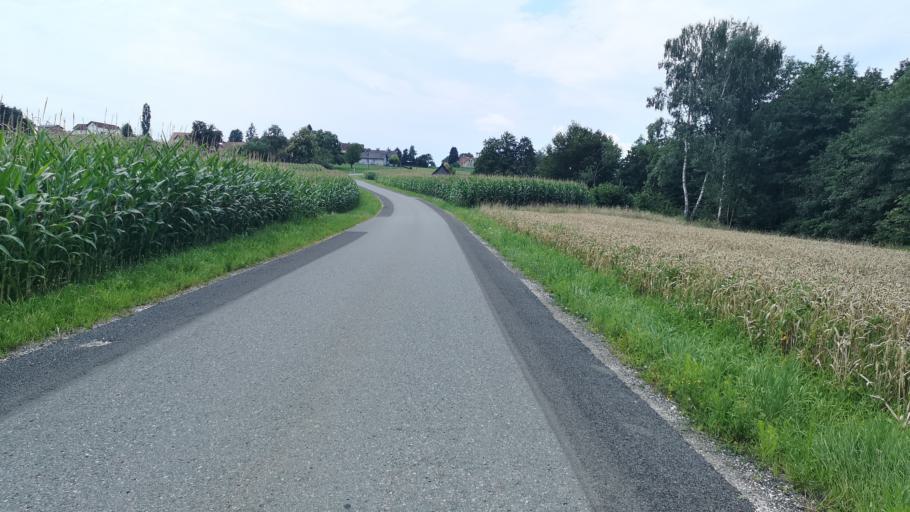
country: AT
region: Styria
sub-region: Politischer Bezirk Leibnitz
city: Weitendorf
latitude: 46.8761
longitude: 15.4613
